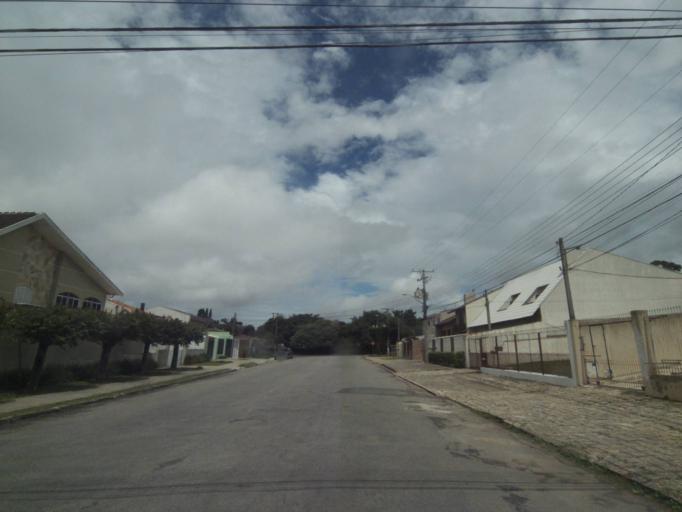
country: BR
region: Parana
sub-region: Curitiba
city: Curitiba
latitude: -25.4871
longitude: -49.2780
